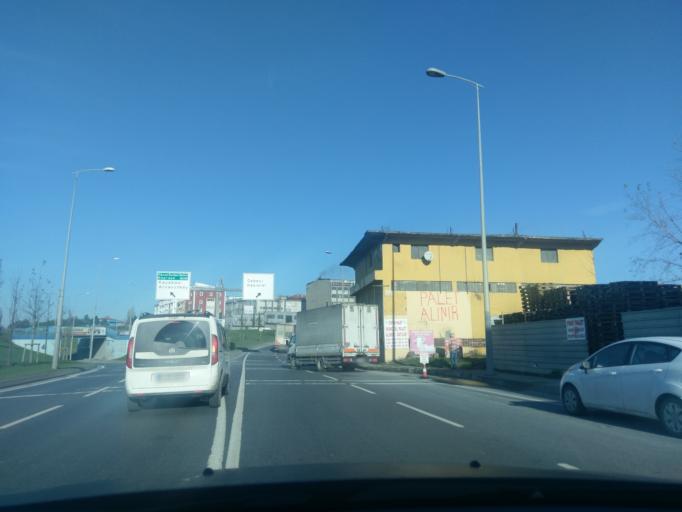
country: TR
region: Istanbul
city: Sultangazi
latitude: 41.1103
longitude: 28.8490
